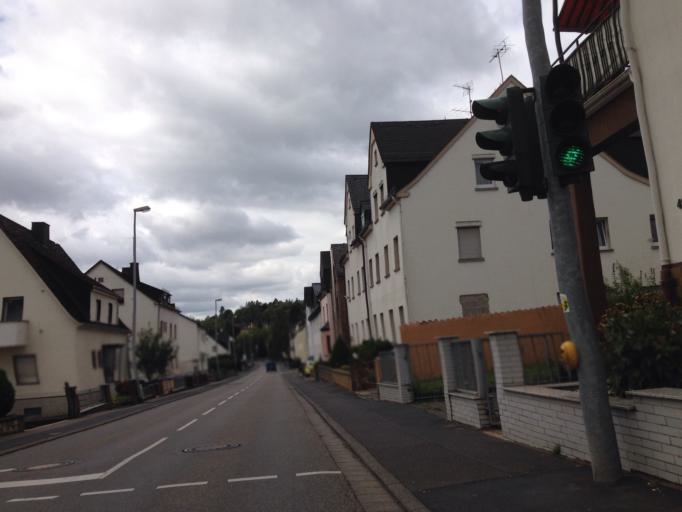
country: DE
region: Hesse
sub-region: Regierungsbezirk Giessen
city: Elz
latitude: 50.4152
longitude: 8.0438
